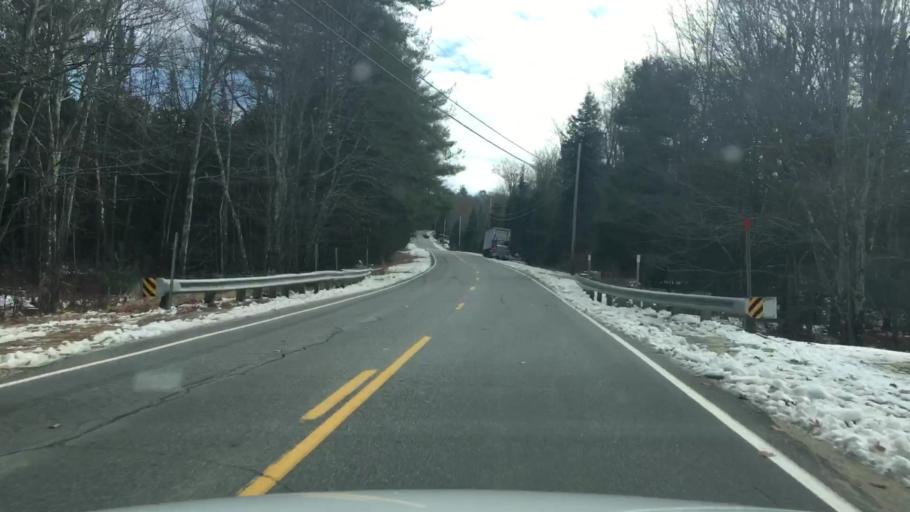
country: US
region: Maine
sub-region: Androscoggin County
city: Livermore
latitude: 44.3888
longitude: -70.2218
